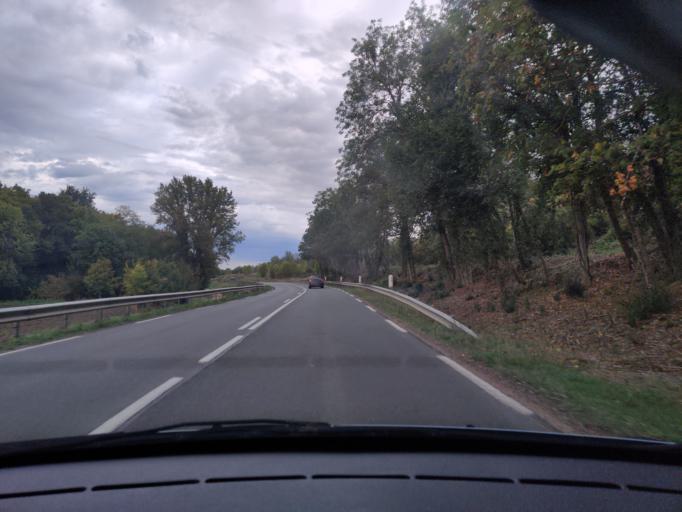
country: FR
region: Auvergne
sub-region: Departement du Puy-de-Dome
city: Riom
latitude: 45.9154
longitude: 3.1225
